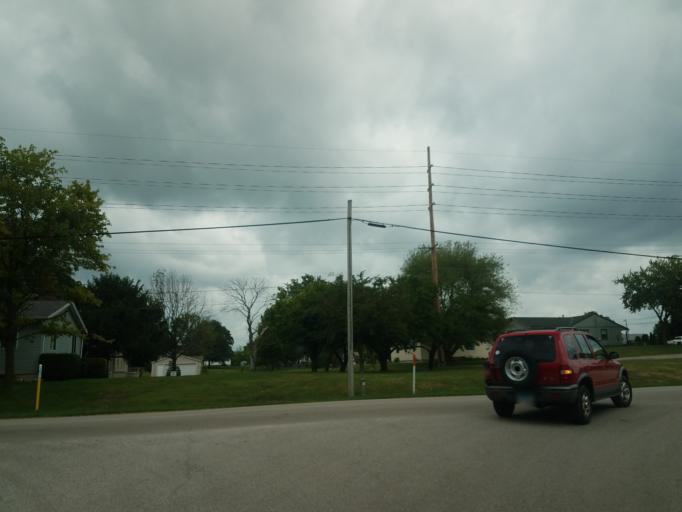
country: US
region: Illinois
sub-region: McLean County
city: Bloomington
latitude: 40.4802
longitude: -89.0330
